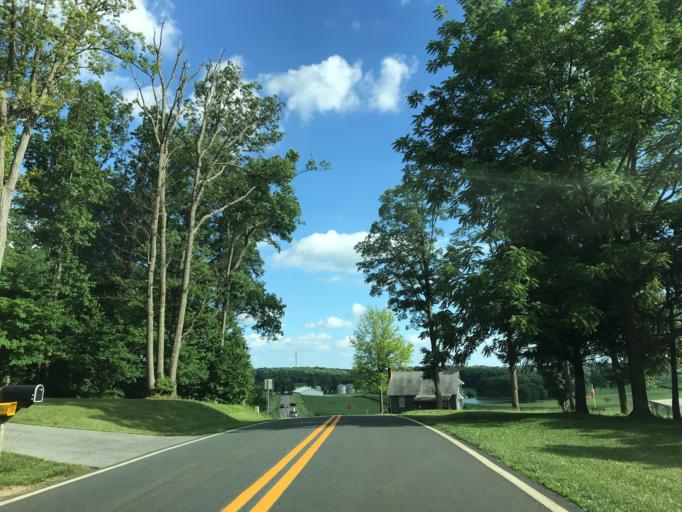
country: US
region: Maryland
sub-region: Carroll County
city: Manchester
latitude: 39.6800
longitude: -76.8245
